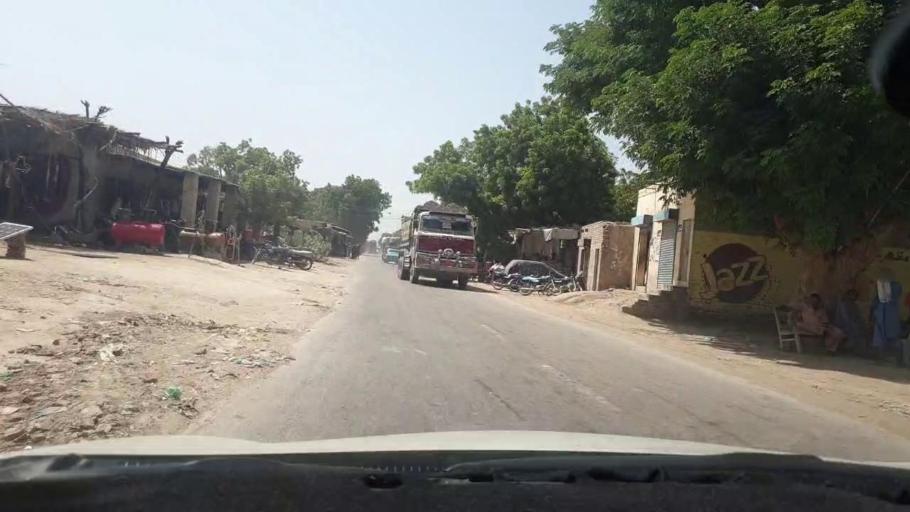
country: PK
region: Sindh
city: Bhit Shah
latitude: 25.8531
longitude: 68.4934
